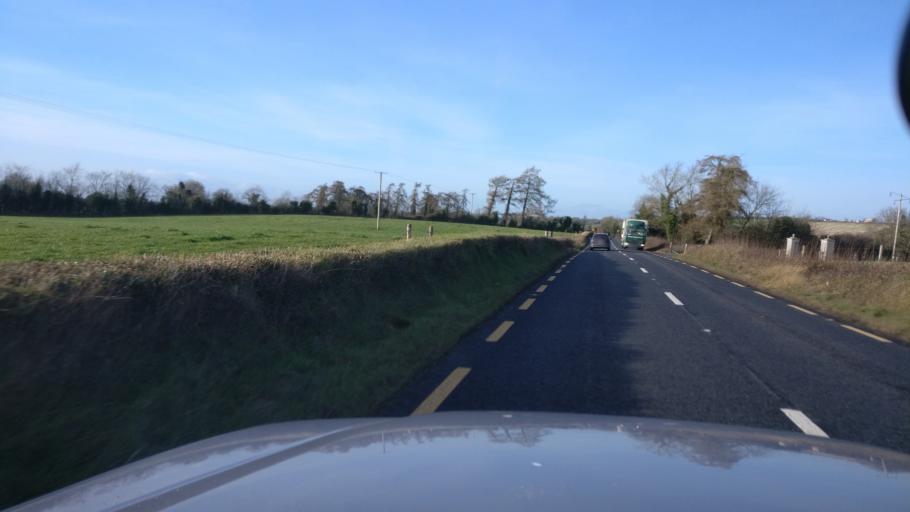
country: IE
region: Leinster
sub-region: Laois
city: Mountmellick
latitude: 53.1862
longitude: -7.4017
